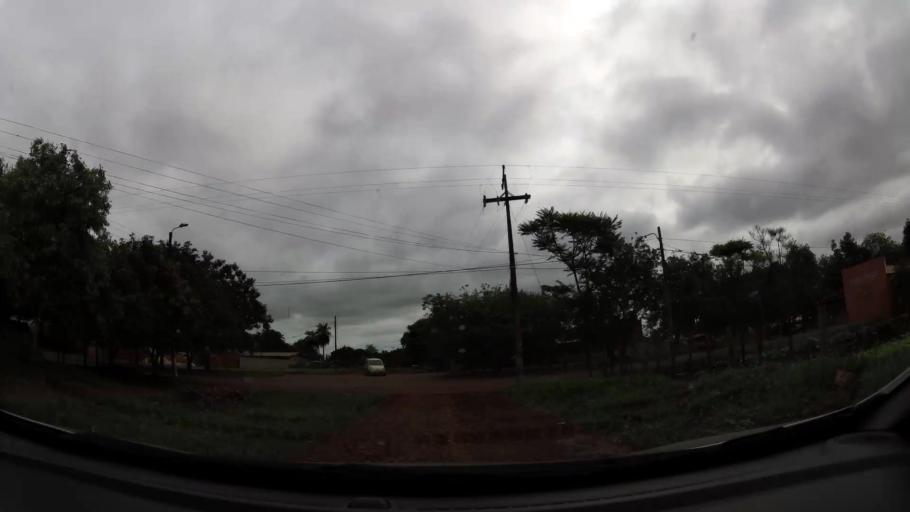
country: PY
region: Alto Parana
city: Ciudad del Este
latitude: -25.3769
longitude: -54.6535
